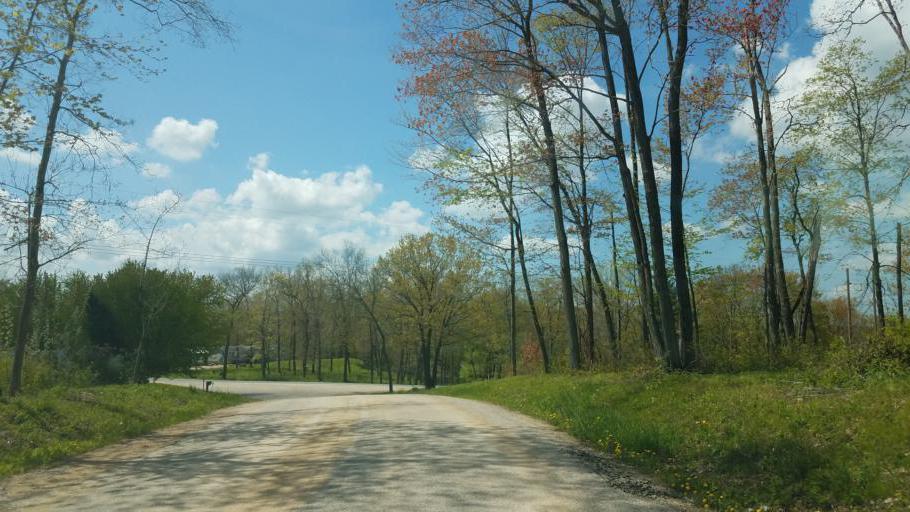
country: US
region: Wisconsin
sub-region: Vernon County
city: Hillsboro
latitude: 43.6921
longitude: -90.3185
